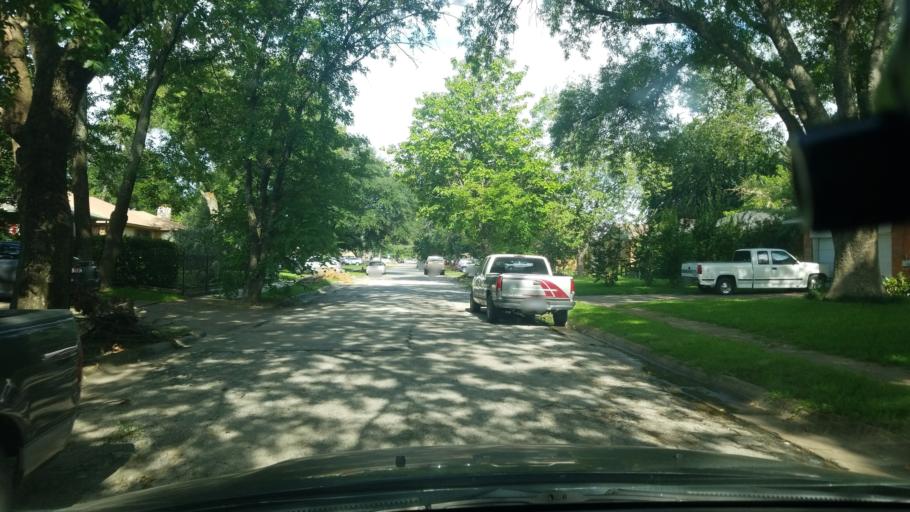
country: US
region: Texas
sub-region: Dallas County
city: Balch Springs
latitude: 32.7477
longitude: -96.6634
